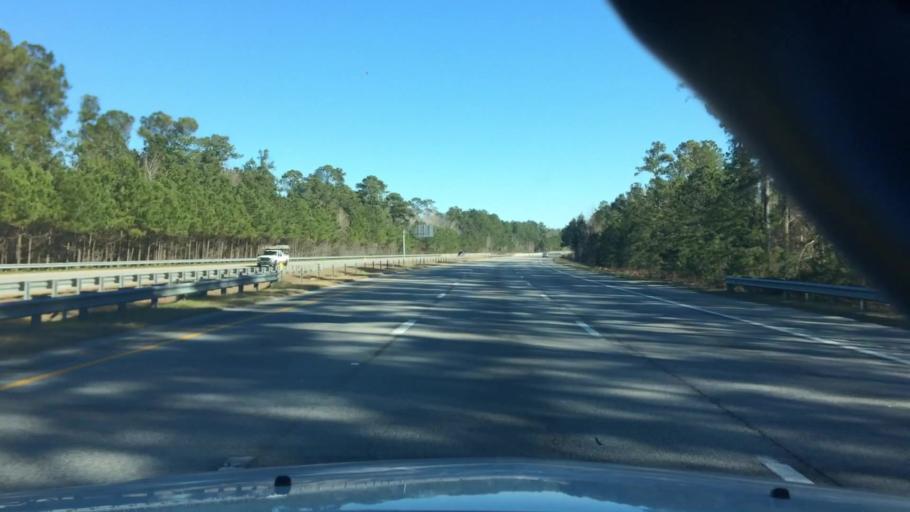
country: US
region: South Carolina
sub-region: Horry County
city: North Myrtle Beach
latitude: 33.8616
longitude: -78.6951
